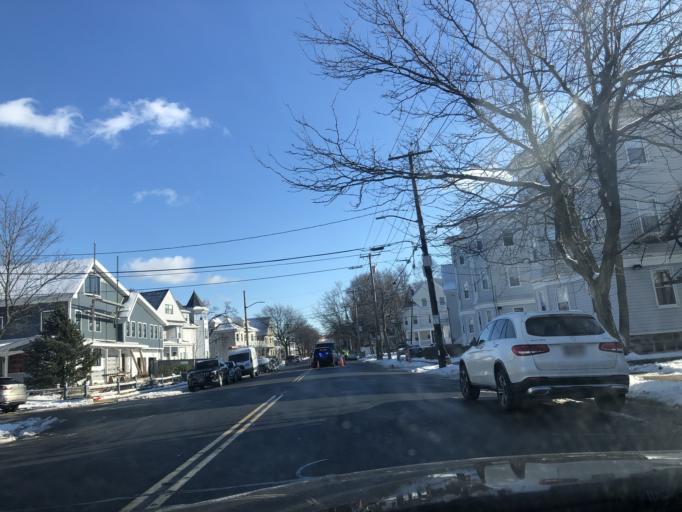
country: US
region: Massachusetts
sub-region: Middlesex County
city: Arlington
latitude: 42.4135
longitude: -71.1482
